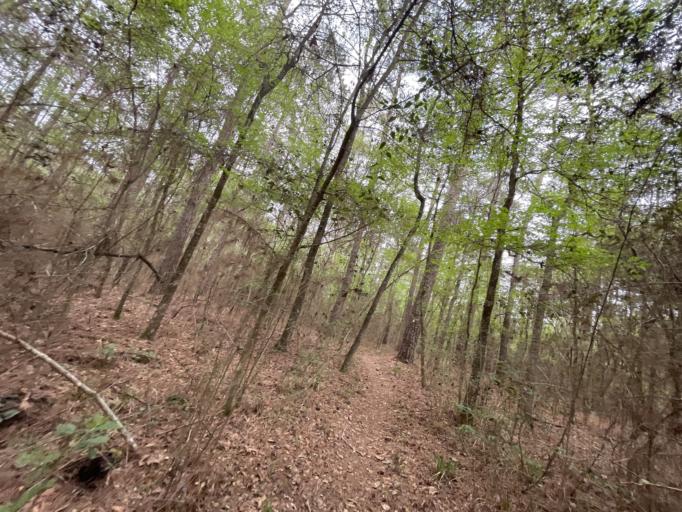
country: US
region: Texas
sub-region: Walker County
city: Huntsville
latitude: 30.6632
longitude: -95.4870
